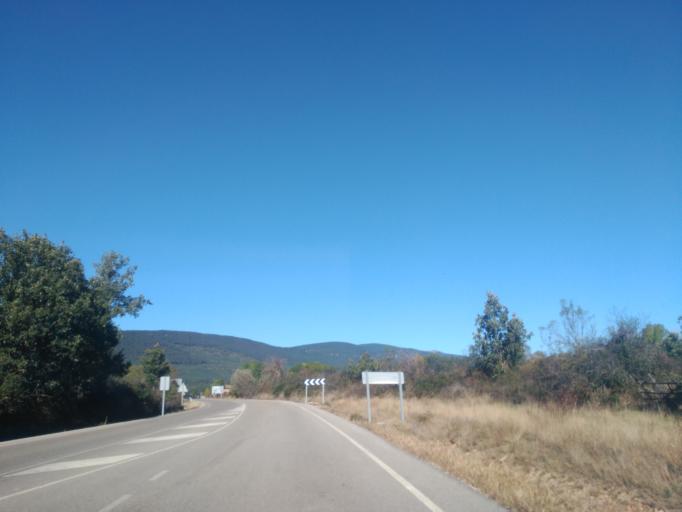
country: ES
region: Castille and Leon
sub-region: Provincia de Soria
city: Vinuesa
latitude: 41.9103
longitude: -2.7516
